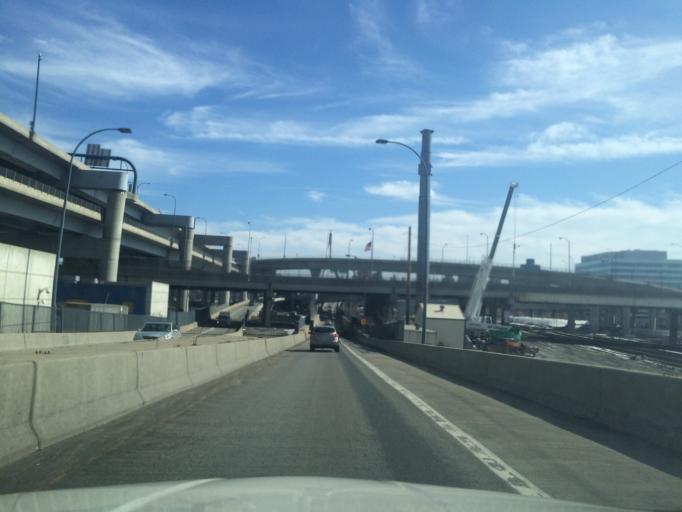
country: US
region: Massachusetts
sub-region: Suffolk County
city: Boston
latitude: 42.3738
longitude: -71.0712
